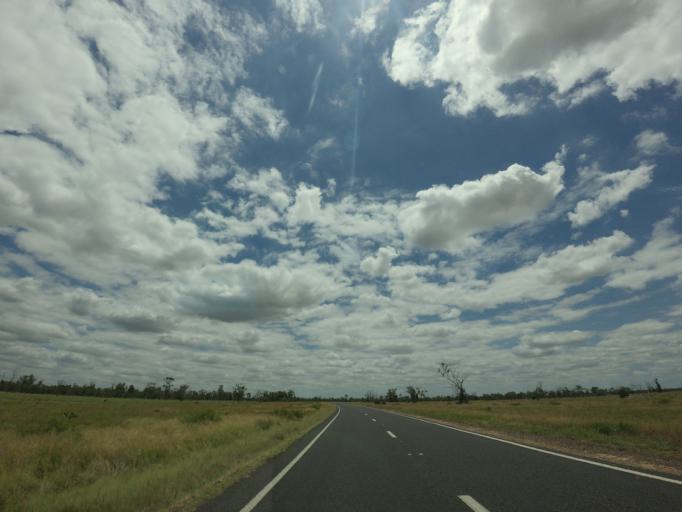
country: AU
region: New South Wales
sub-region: Moree Plains
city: Boggabilla
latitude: -28.6488
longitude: 150.3404
